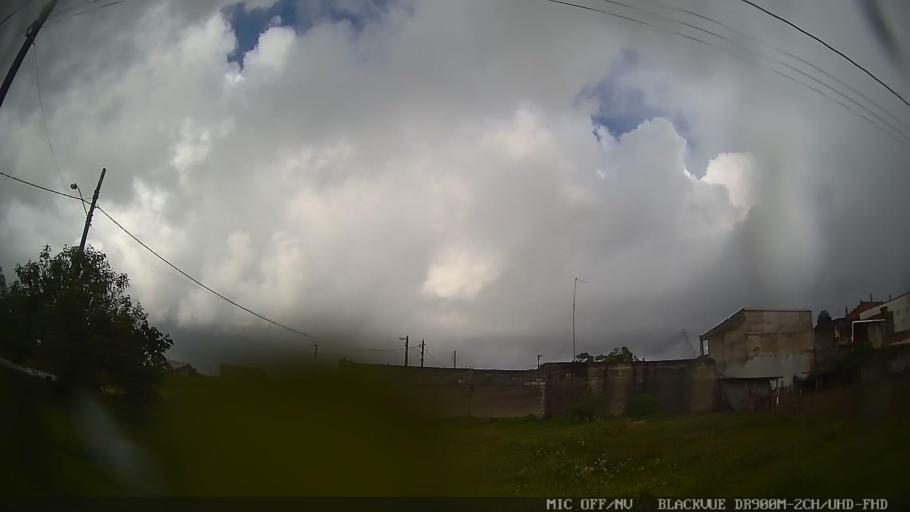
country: BR
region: Sao Paulo
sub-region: Peruibe
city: Peruibe
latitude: -24.2480
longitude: -46.8982
